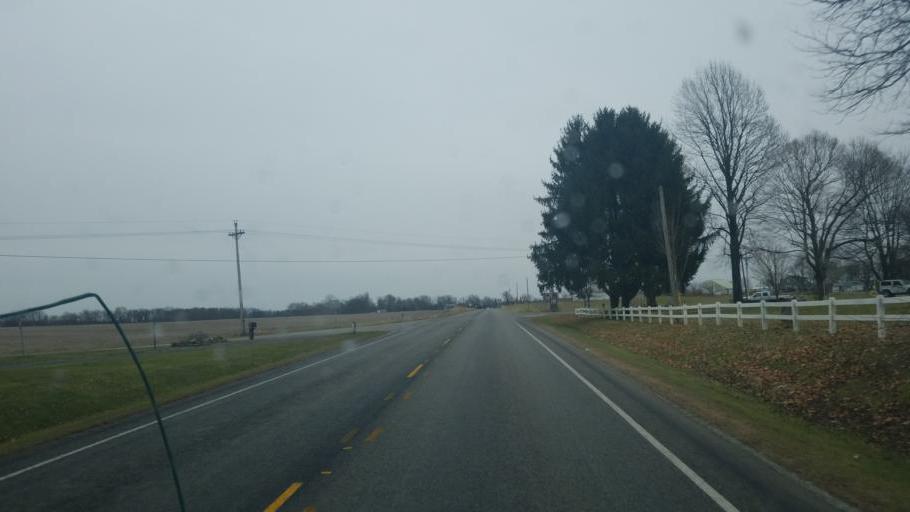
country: US
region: Indiana
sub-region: Henry County
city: Knightstown
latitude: 39.8292
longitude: -85.5426
